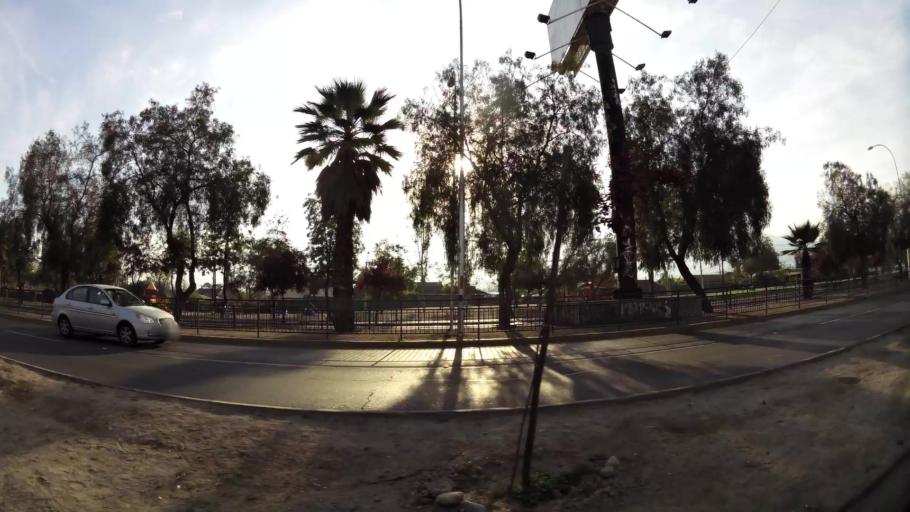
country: CL
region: Santiago Metropolitan
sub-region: Provincia de Santiago
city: Villa Presidente Frei, Nunoa, Santiago, Chile
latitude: -33.5251
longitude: -70.5778
